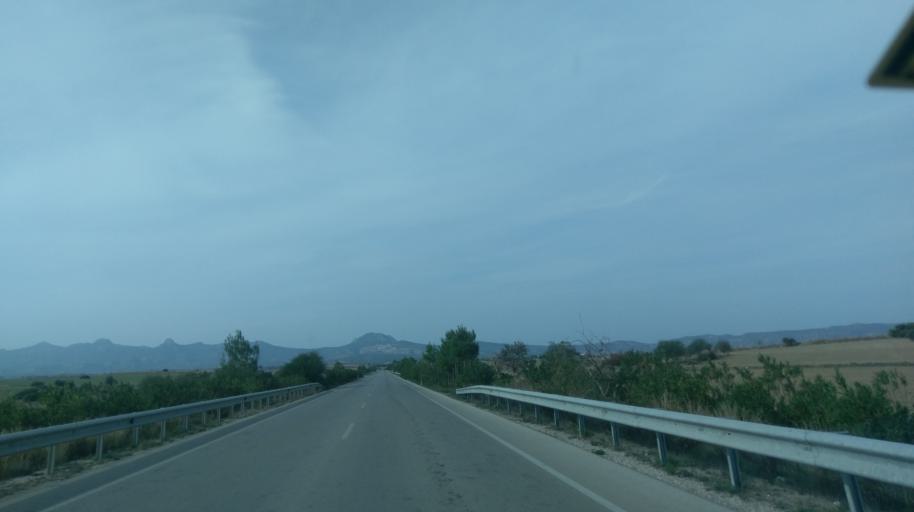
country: CY
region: Ammochostos
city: Leonarisso
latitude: 35.3789
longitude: 34.0238
